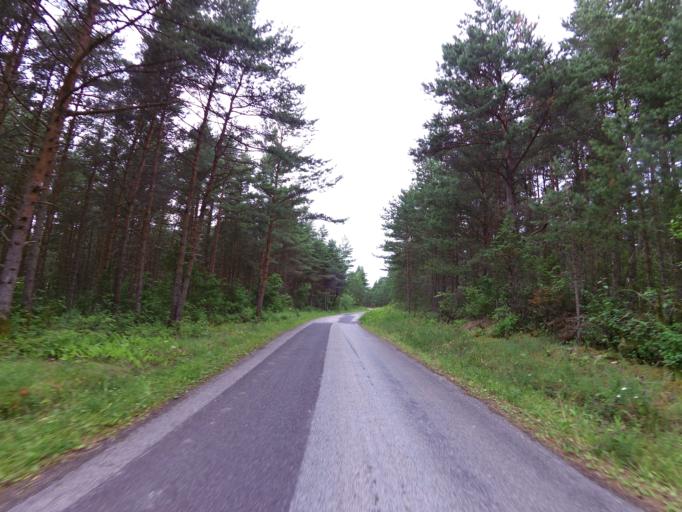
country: EE
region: Laeaene
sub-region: Vormsi vald
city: Hullo
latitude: 58.9763
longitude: 23.2577
